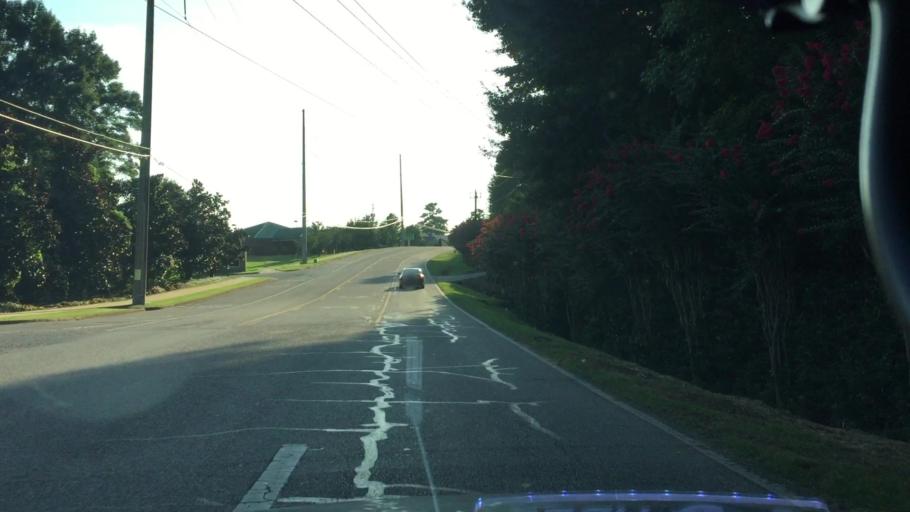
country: US
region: Alabama
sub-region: Lee County
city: Auburn
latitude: 32.5847
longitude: -85.4419
